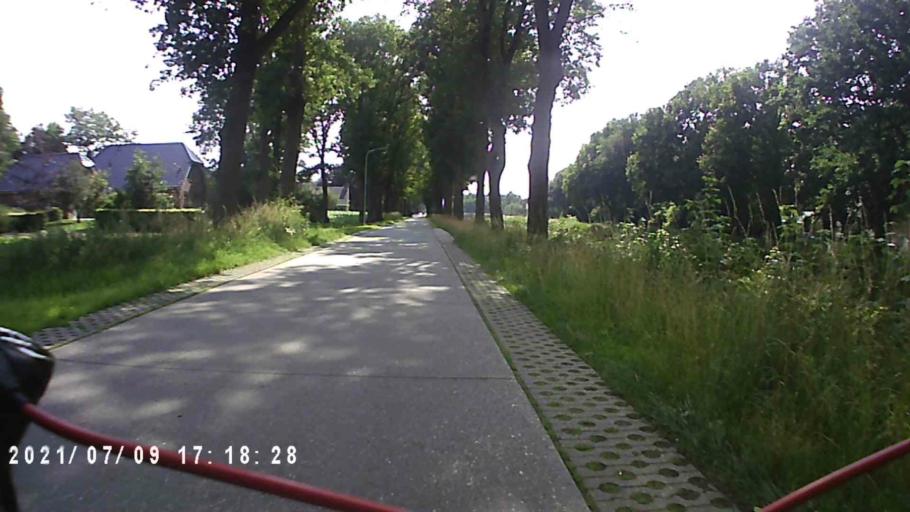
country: NL
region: Groningen
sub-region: Gemeente Vlagtwedde
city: Vlagtwedde
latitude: 53.0902
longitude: 7.1723
